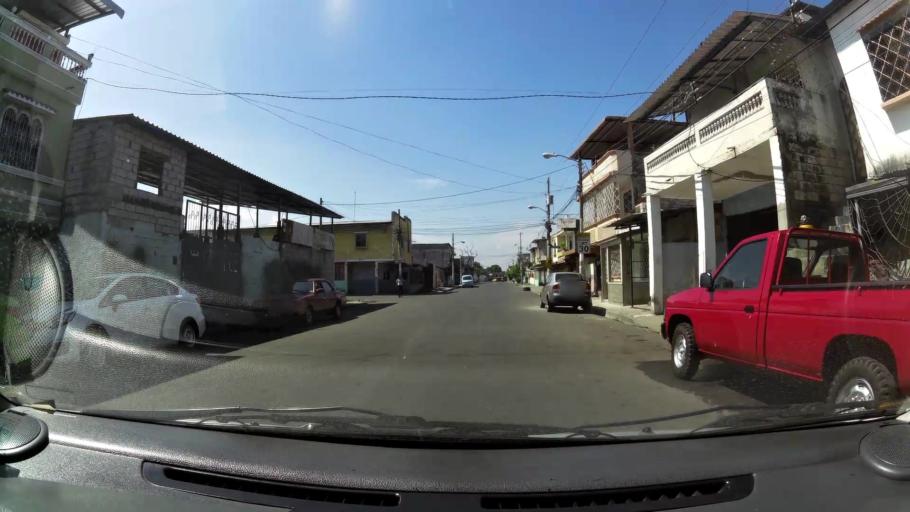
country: EC
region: Guayas
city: Guayaquil
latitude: -2.2256
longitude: -79.9374
